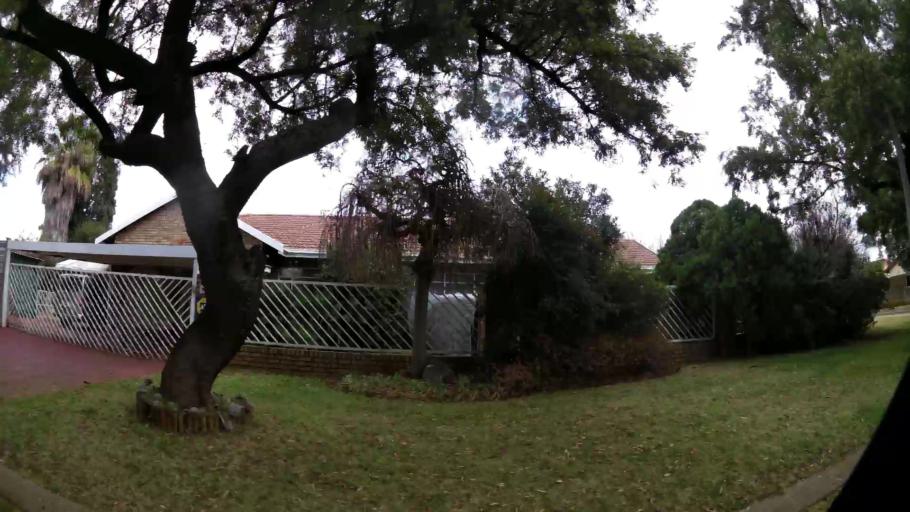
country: ZA
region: Gauteng
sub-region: Sedibeng District Municipality
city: Vanderbijlpark
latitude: -26.7297
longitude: 27.8551
